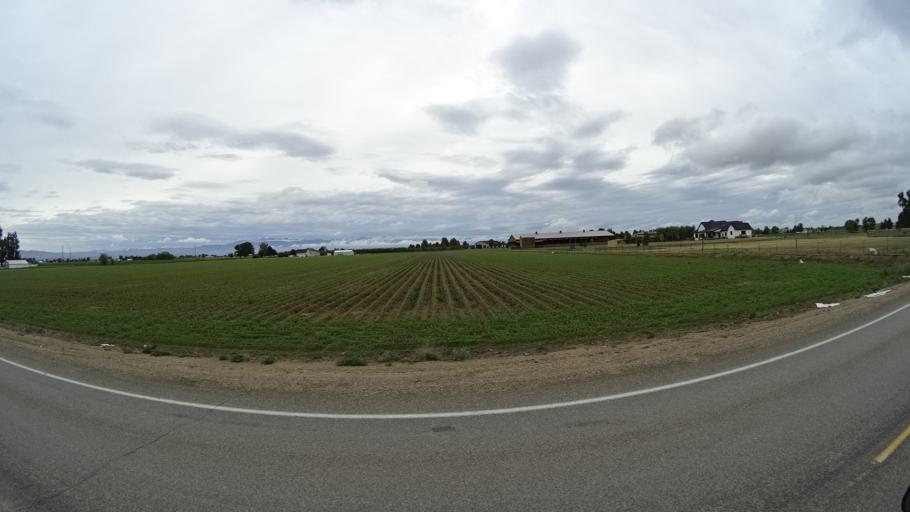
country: US
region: Idaho
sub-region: Ada County
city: Star
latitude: 43.6543
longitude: -116.4938
